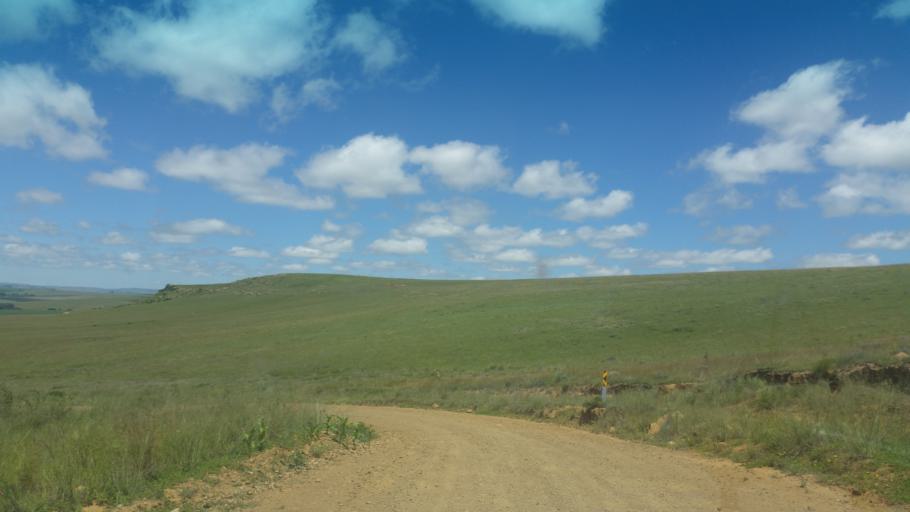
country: ZA
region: Orange Free State
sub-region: Thabo Mofutsanyana District Municipality
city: Harrismith
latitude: -28.2063
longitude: 28.9770
